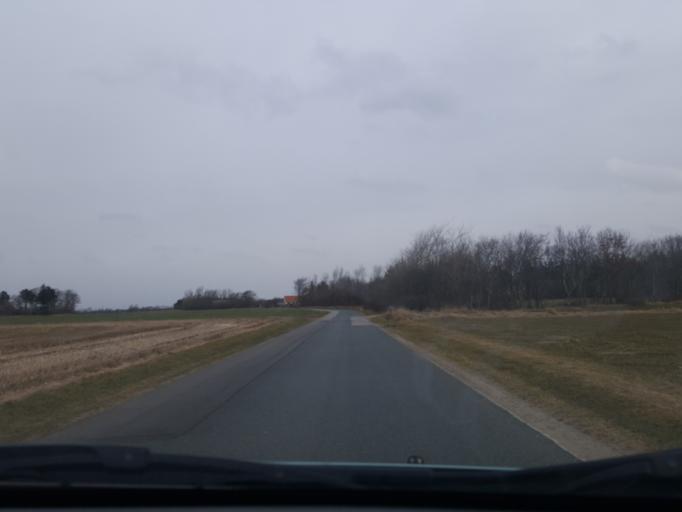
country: DK
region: Central Jutland
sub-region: Holstebro Kommune
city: Ulfborg
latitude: 56.2129
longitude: 8.2597
